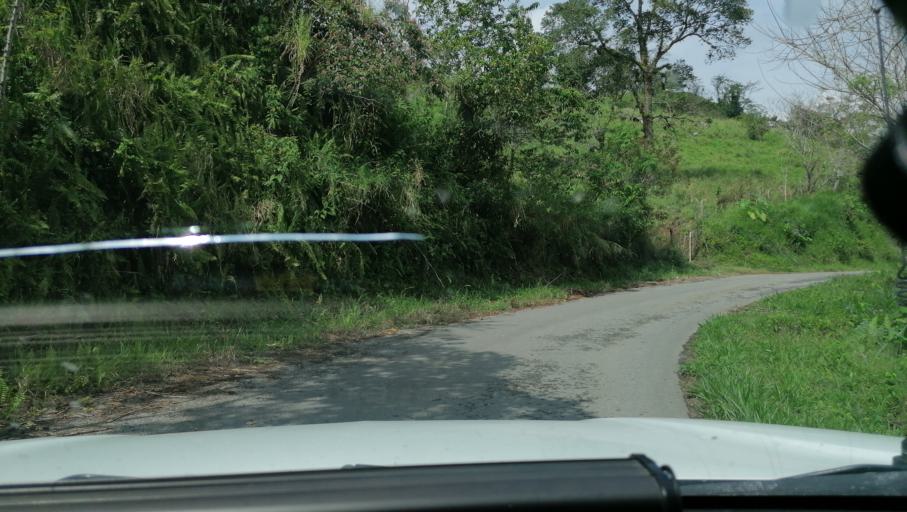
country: MX
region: Chiapas
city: Ocotepec
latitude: 17.3132
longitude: -93.1729
